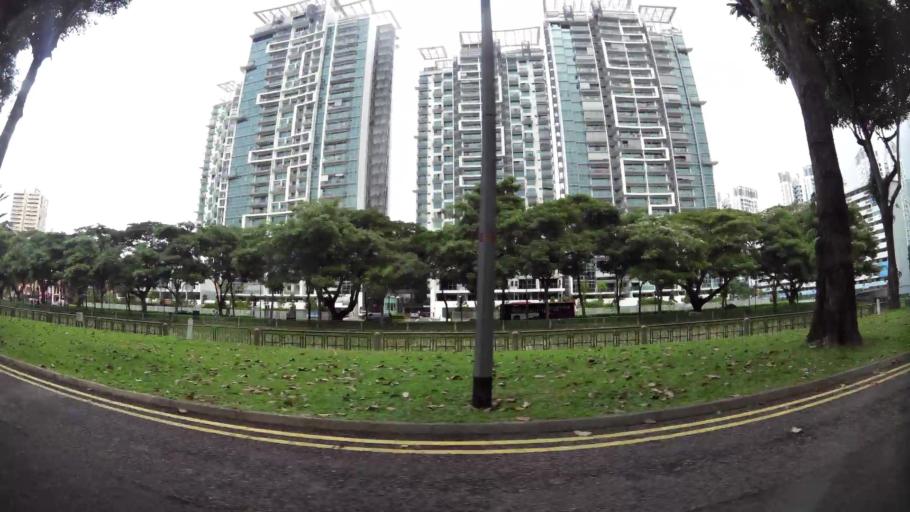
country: SG
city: Singapore
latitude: 1.3205
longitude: 103.8640
